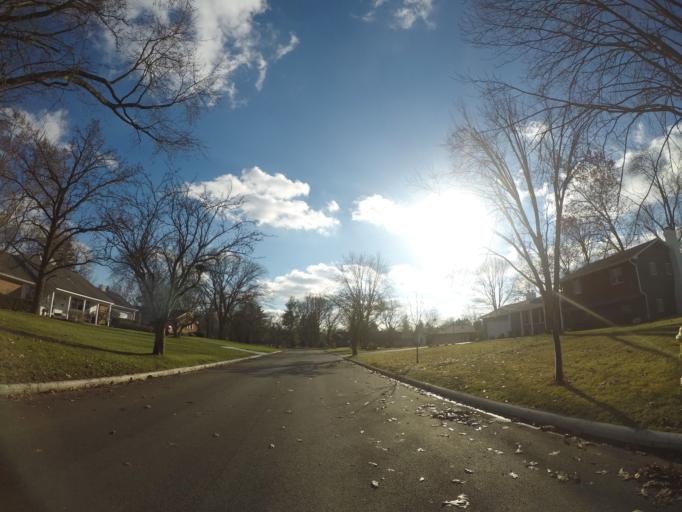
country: US
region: Ohio
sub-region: Franklin County
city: Upper Arlington
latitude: 40.0331
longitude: -83.0823
